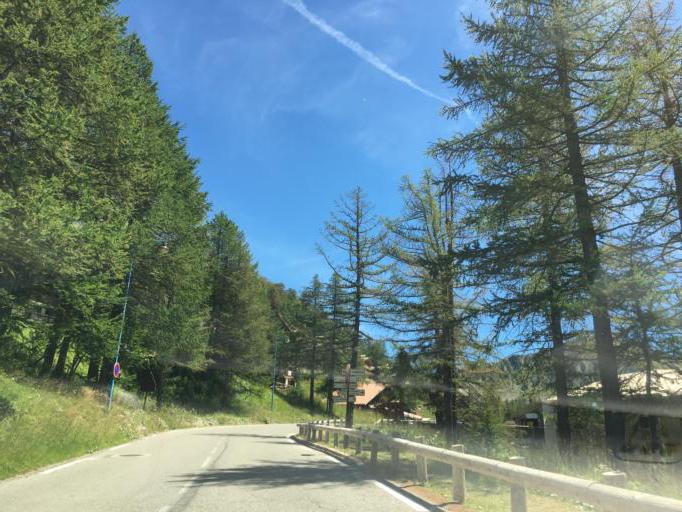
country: IT
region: Piedmont
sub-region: Provincia di Cuneo
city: Vinadio
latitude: 44.1882
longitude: 7.1584
